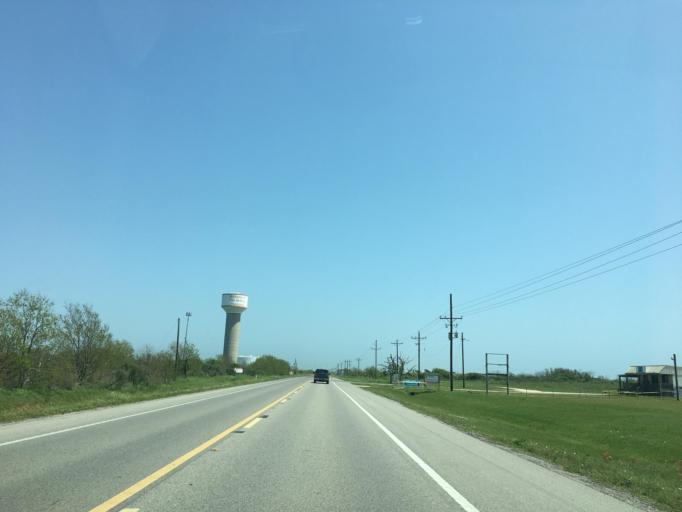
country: US
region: Texas
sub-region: Galveston County
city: Bolivar Peninsula
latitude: 29.4197
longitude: -94.7050
